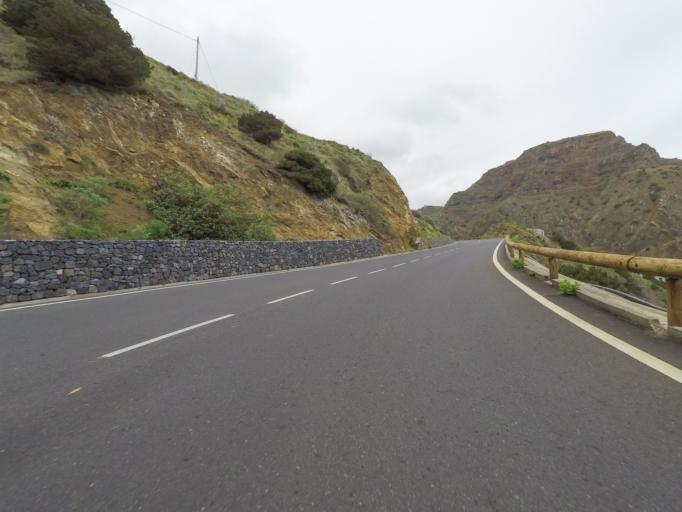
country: ES
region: Canary Islands
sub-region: Provincia de Santa Cruz de Tenerife
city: Agulo
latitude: 28.1906
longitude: -17.2040
